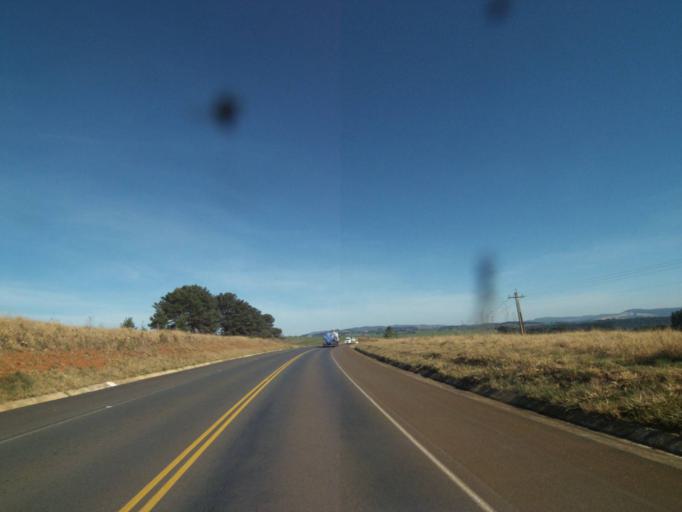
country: BR
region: Parana
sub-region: Tibagi
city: Tibagi
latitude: -24.4568
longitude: -50.4240
